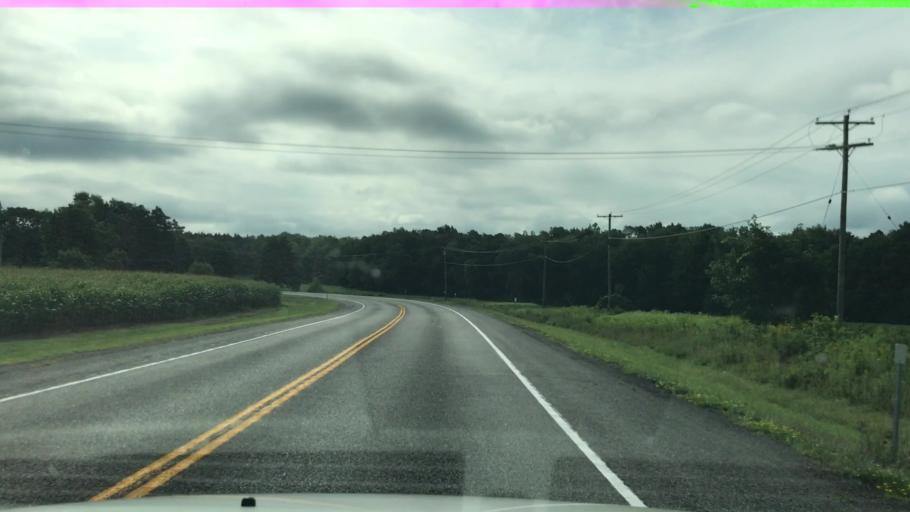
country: US
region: New York
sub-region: Erie County
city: Alden
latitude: 42.8357
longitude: -78.4503
